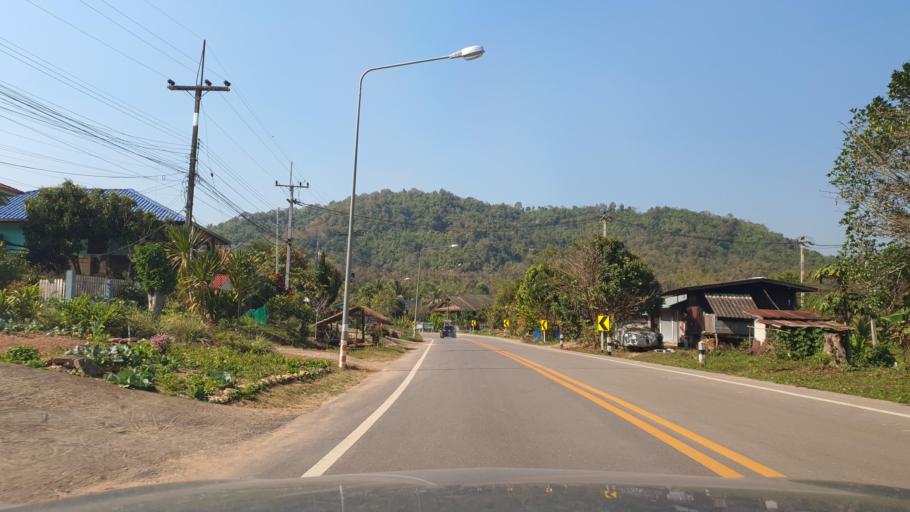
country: TH
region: Chiang Rai
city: Mae Lao
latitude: 19.8374
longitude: 99.6811
